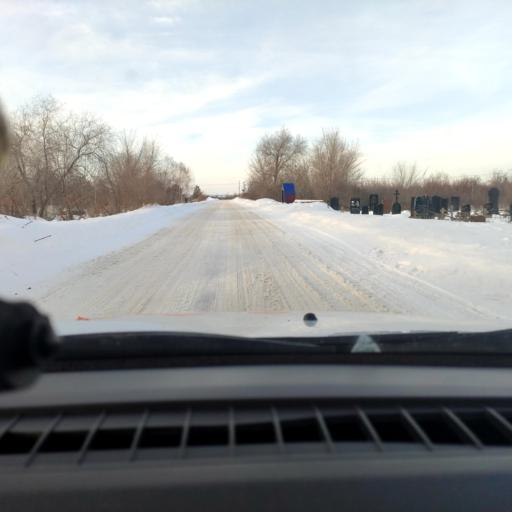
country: RU
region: Samara
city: Chapayevsk
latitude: 52.9909
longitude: 49.7437
